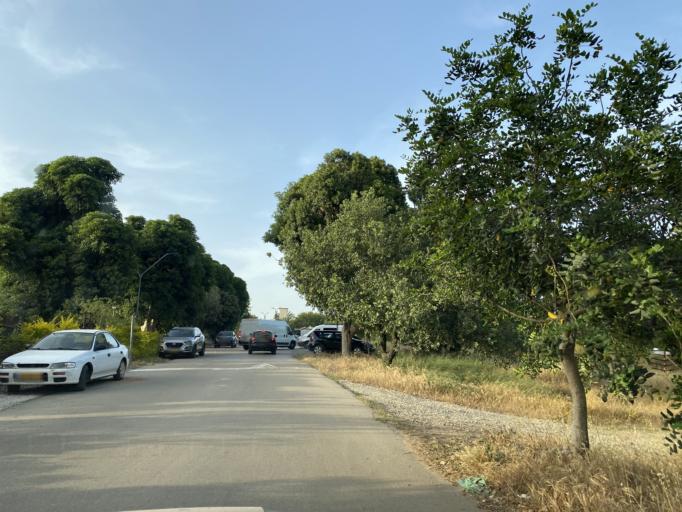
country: IL
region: Tel Aviv
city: Ramat HaSharon
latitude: 32.1552
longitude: 34.8314
